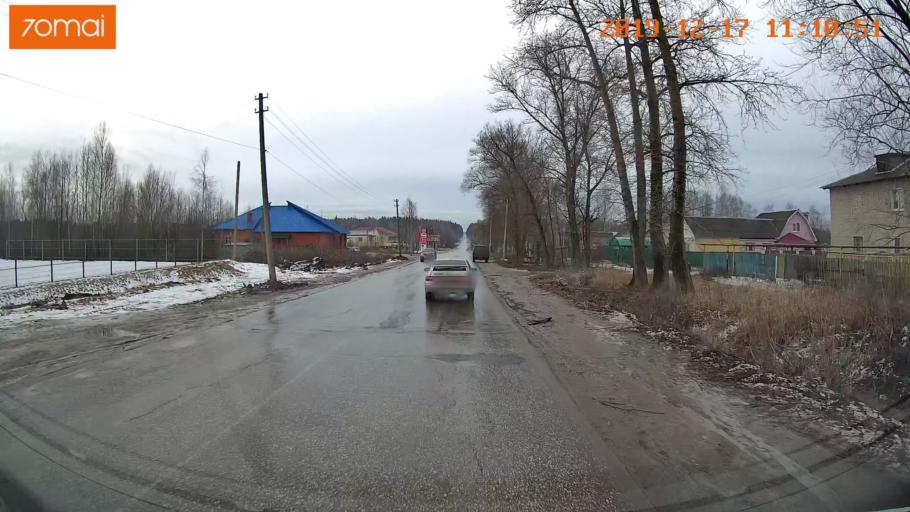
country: RU
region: Vladimir
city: Gus'-Khrustal'nyy
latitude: 55.5900
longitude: 40.6394
